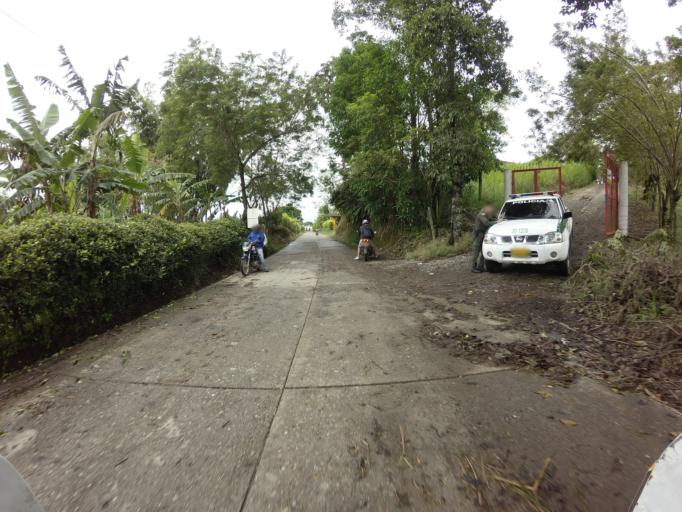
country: CO
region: Valle del Cauca
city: Ulloa
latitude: 4.6998
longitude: -75.7479
